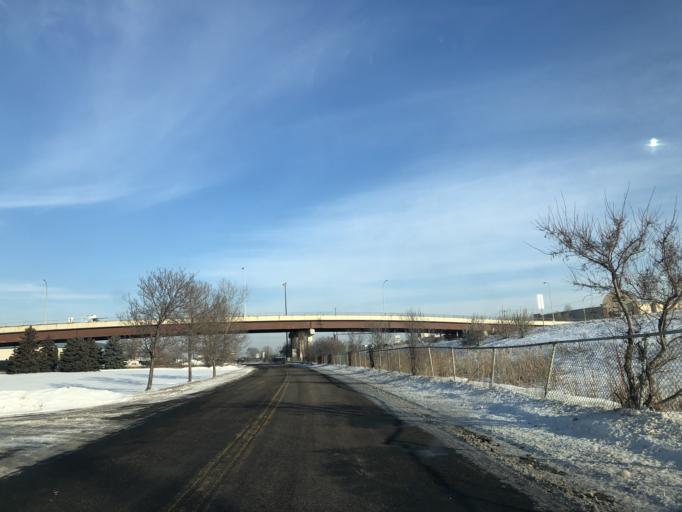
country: US
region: Minnesota
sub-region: Ramsey County
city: Lauderdale
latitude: 45.0134
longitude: -93.1882
